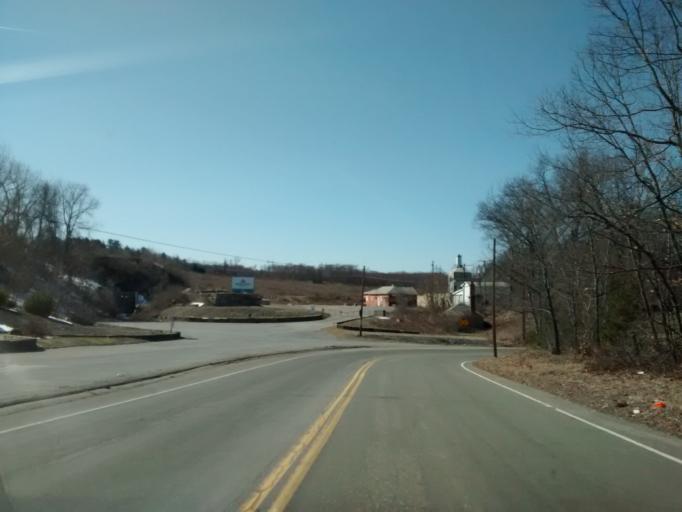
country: US
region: Massachusetts
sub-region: Worcester County
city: Millbury
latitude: 42.1799
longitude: -71.7327
